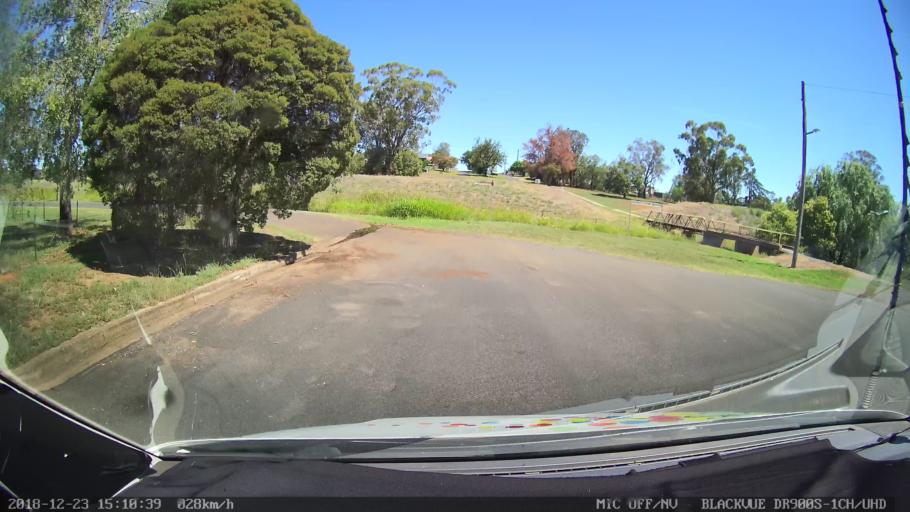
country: AU
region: New South Wales
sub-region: Tamworth Municipality
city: Manilla
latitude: -30.7513
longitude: 150.7220
